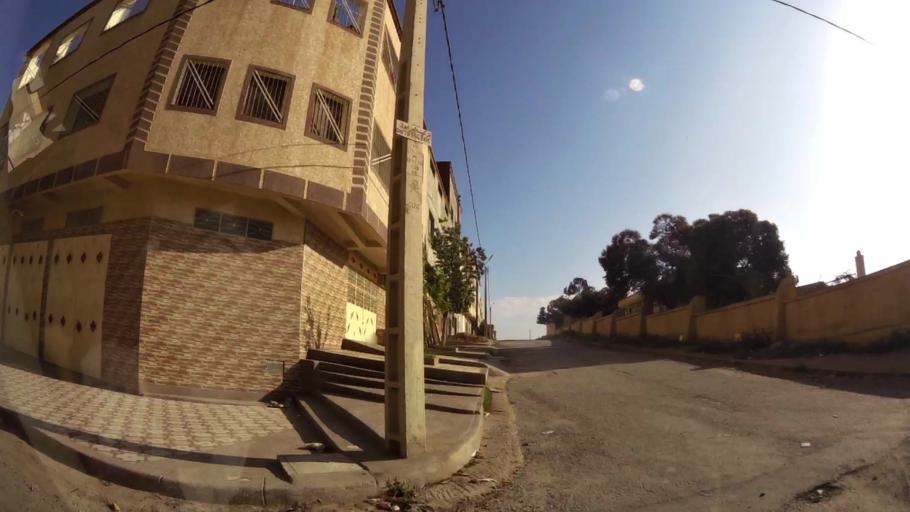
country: MA
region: Oriental
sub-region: Oujda-Angad
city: Oujda
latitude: 34.6751
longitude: -1.9423
